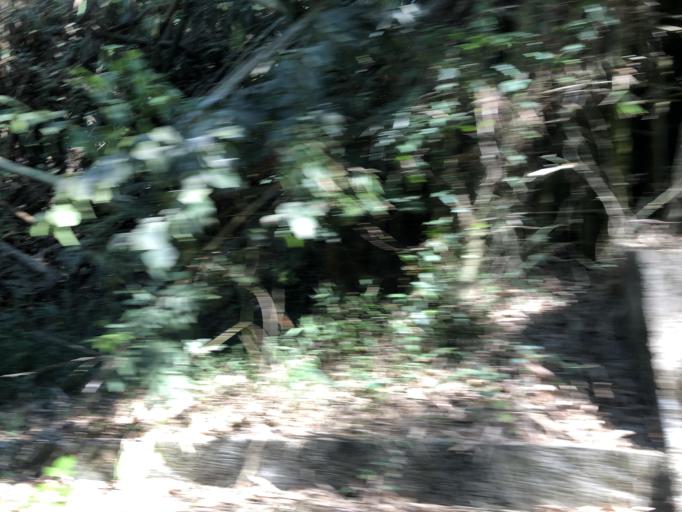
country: TW
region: Taiwan
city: Yujing
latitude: 23.0618
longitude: 120.3816
